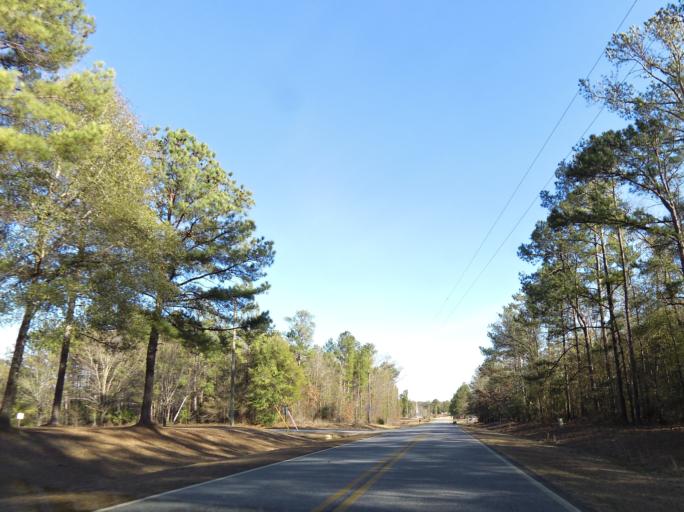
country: US
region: Georgia
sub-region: Bibb County
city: West Point
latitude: 32.7668
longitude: -83.8530
